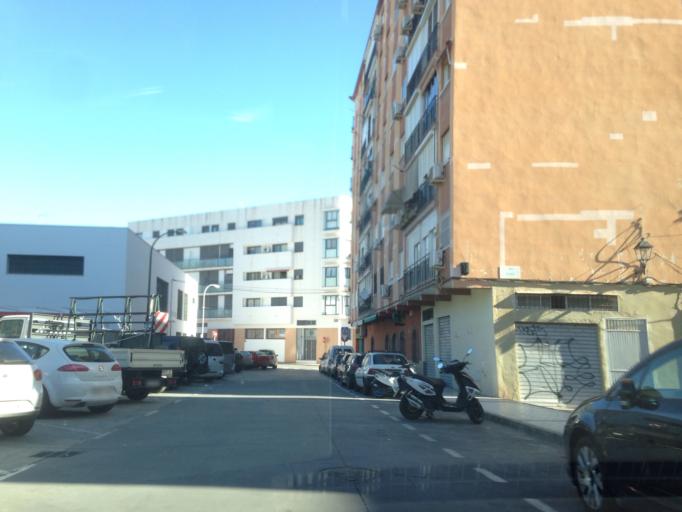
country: ES
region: Andalusia
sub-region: Provincia de Malaga
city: Malaga
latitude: 36.7277
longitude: -4.4155
